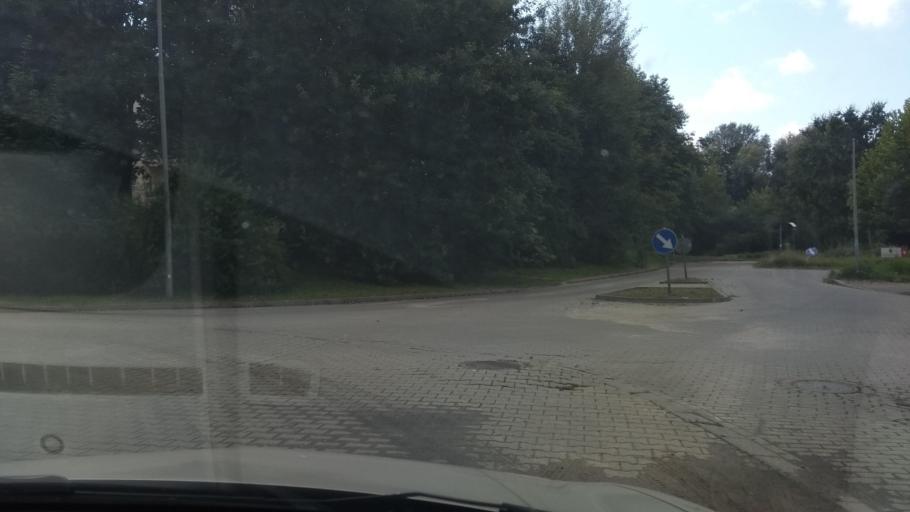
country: PL
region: Masovian Voivodeship
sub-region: Powiat pruszkowski
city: Pruszkow
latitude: 52.1626
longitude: 20.8210
